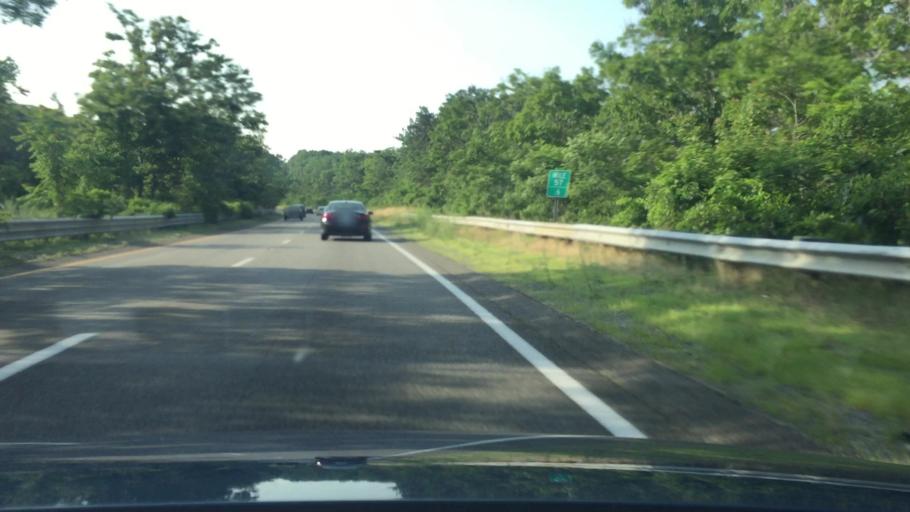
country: US
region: Massachusetts
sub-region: Barnstable County
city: Sandwich
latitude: 41.7483
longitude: -70.5143
